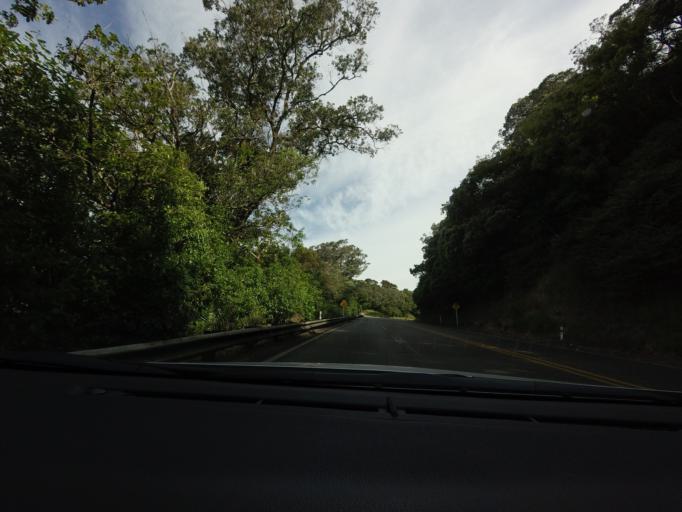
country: NZ
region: Auckland
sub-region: Auckland
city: Warkworth
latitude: -36.5485
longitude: 174.7061
